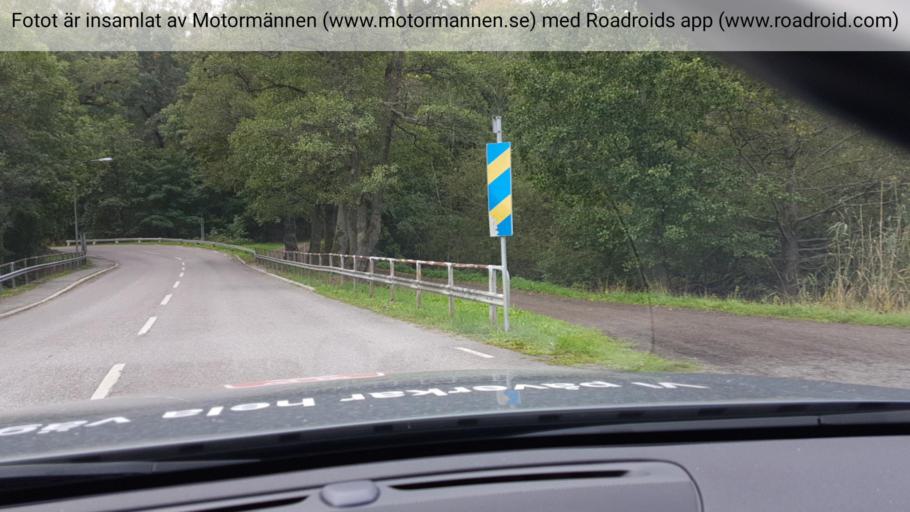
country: SE
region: Stockholm
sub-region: Stockholms Kommun
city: OEstermalm
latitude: 59.3563
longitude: 18.0837
